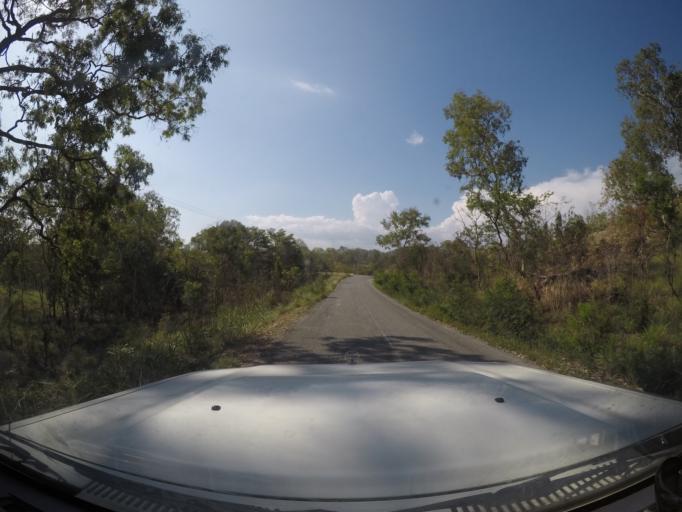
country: PG
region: Central Province
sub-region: Rigo
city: Kwikila
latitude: -9.8660
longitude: 147.5630
